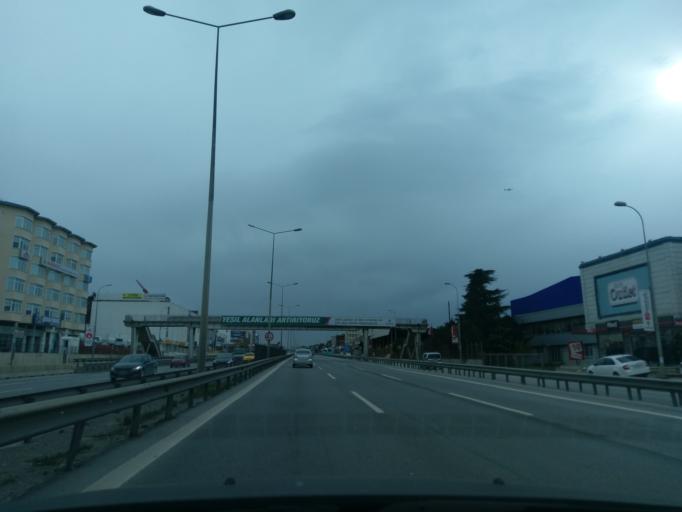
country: TR
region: Istanbul
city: Pendik
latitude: 40.8931
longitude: 29.2313
